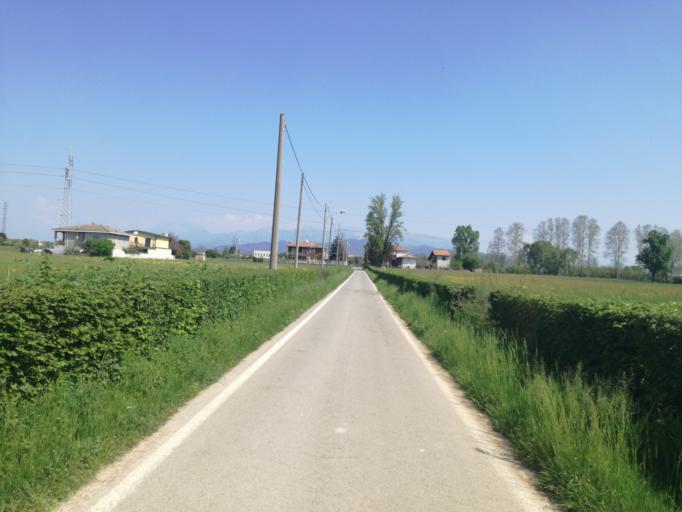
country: IT
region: Lombardy
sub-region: Provincia di Lecco
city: Verderio Superiore
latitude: 45.6562
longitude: 9.4448
